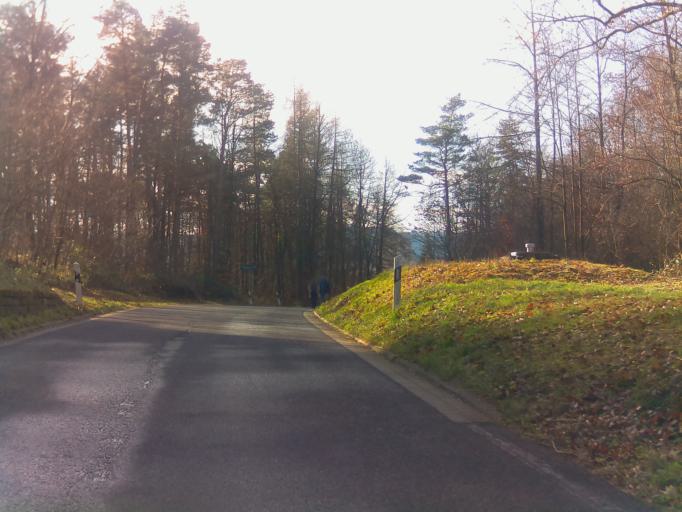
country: DE
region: Bavaria
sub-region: Regierungsbezirk Unterfranken
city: Stadtprozelten
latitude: 49.7947
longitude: 9.4107
